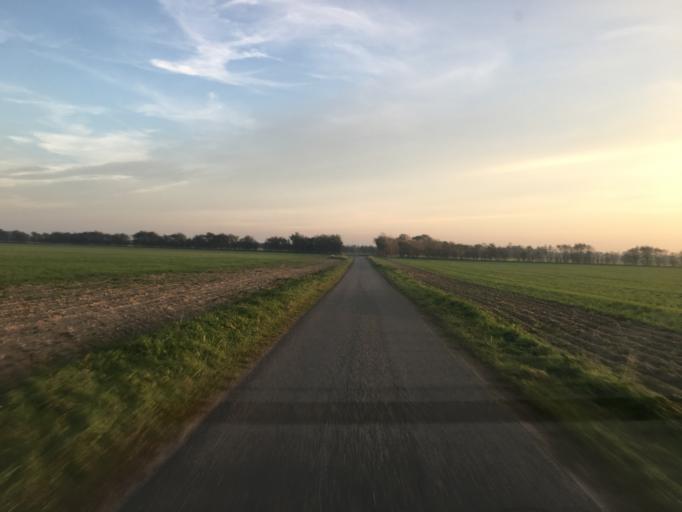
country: DK
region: South Denmark
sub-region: Aabenraa Kommune
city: Tinglev
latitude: 55.0253
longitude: 9.1278
